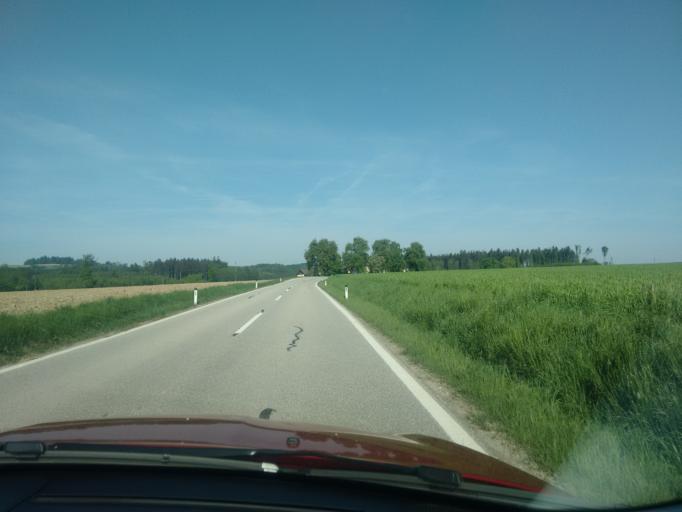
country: AT
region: Upper Austria
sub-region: Politischer Bezirk Grieskirchen
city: Grieskirchen
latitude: 48.3367
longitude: 13.8229
